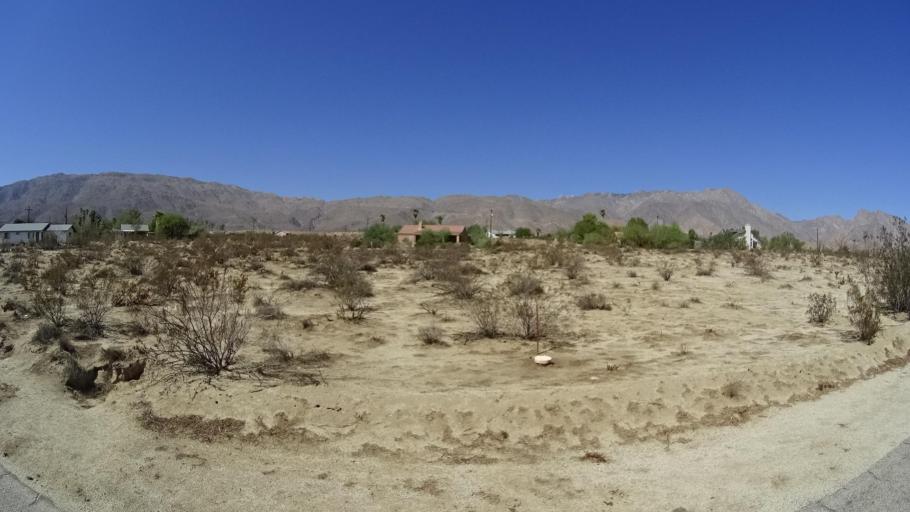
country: US
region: California
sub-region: San Diego County
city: Borrego Springs
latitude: 33.2292
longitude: -116.3706
